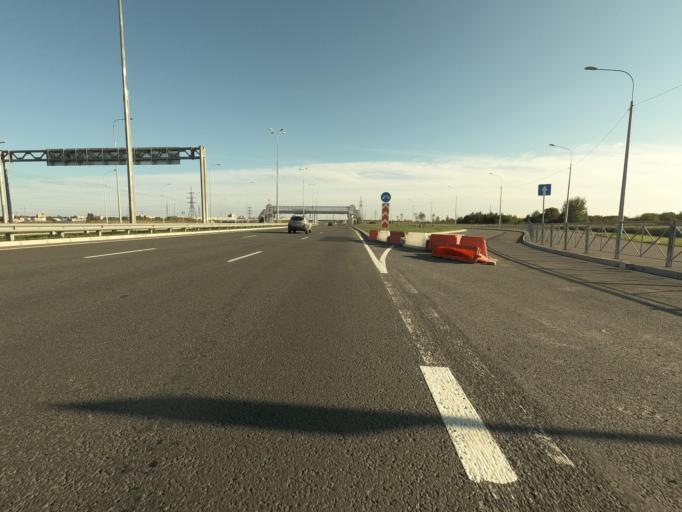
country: RU
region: St.-Petersburg
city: Kolpino
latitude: 59.7471
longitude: 30.5334
